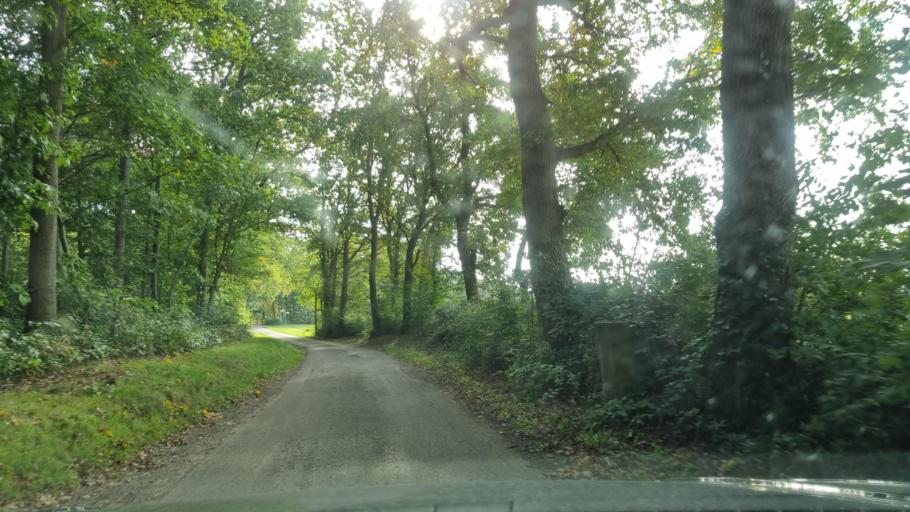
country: DE
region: North Rhine-Westphalia
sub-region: Regierungsbezirk Dusseldorf
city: Kranenburg
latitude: 51.7737
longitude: 6.0633
